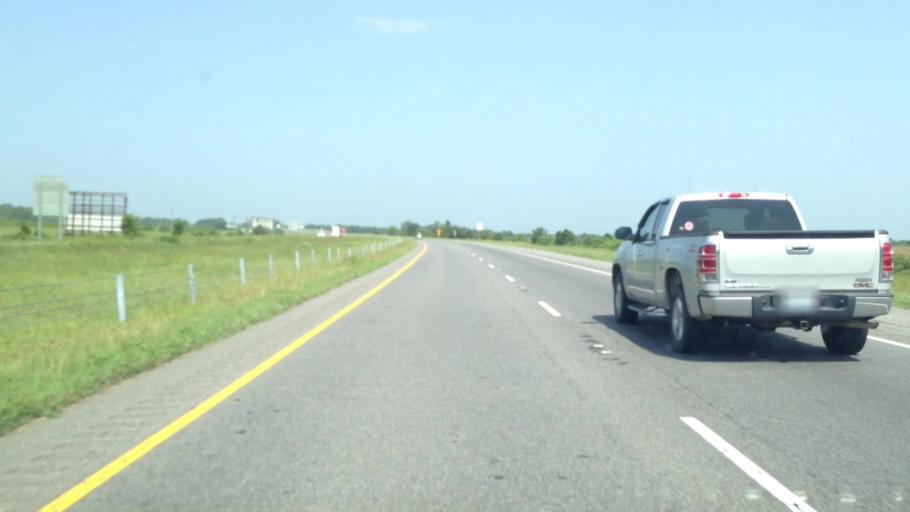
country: US
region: Louisiana
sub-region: Madison Parish
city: Tallulah
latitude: 32.4010
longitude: -91.2149
